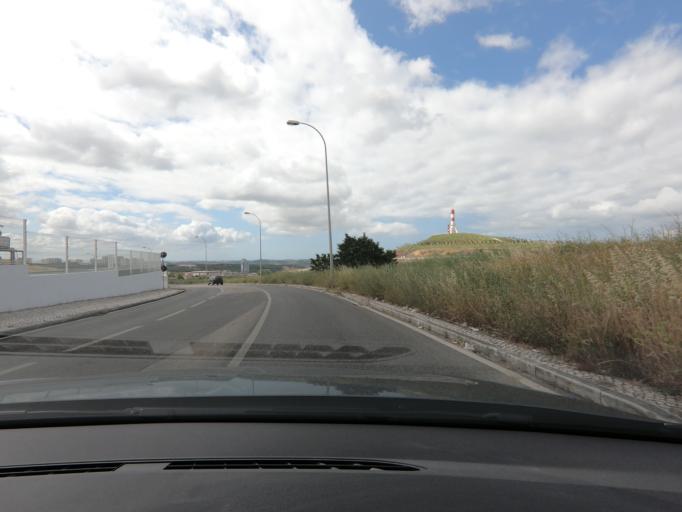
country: PT
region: Lisbon
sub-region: Oeiras
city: Carnaxide
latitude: 38.7305
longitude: -9.2256
